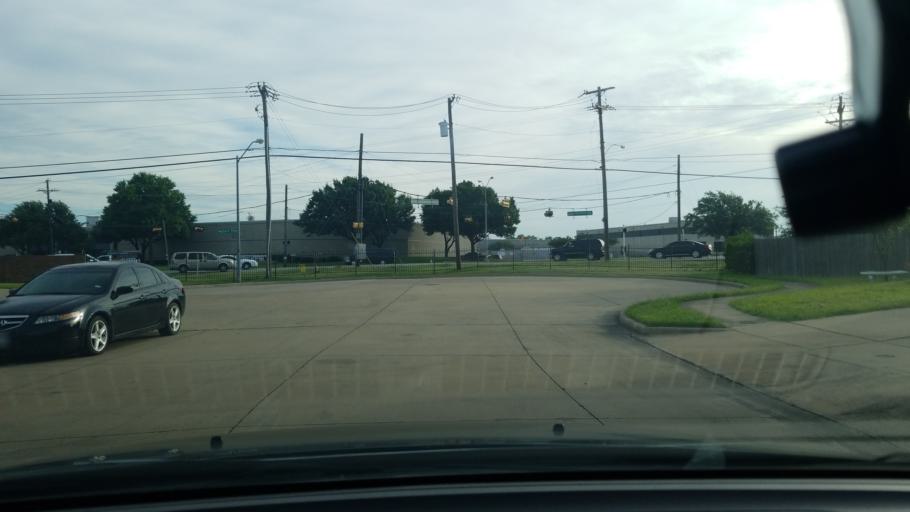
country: US
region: Texas
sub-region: Dallas County
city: Balch Springs
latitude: 32.7677
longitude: -96.6503
